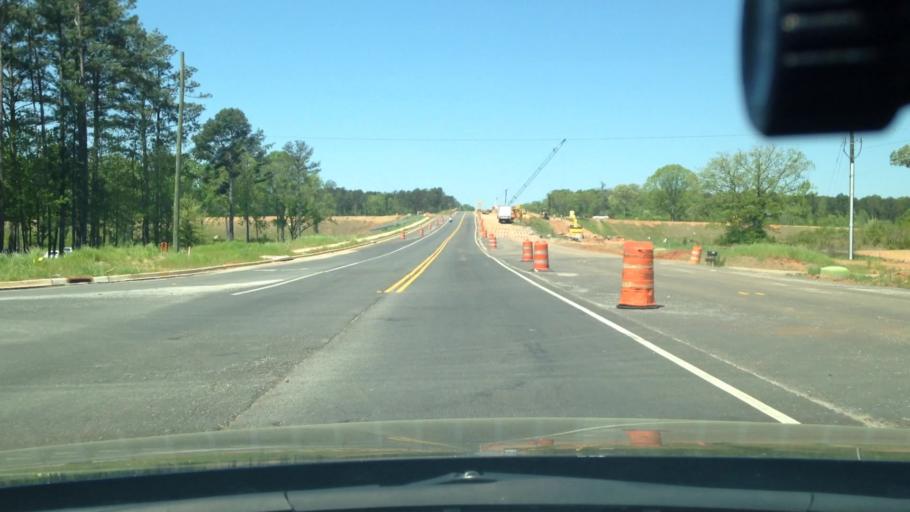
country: US
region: Georgia
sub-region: Coweta County
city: East Newnan
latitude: 33.3595
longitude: -84.7554
